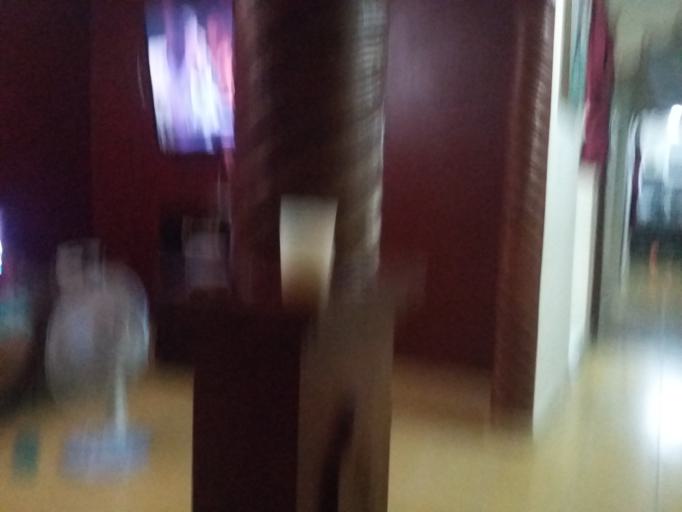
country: CU
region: Granma
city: Bayamo
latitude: 20.3760
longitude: -76.6426
